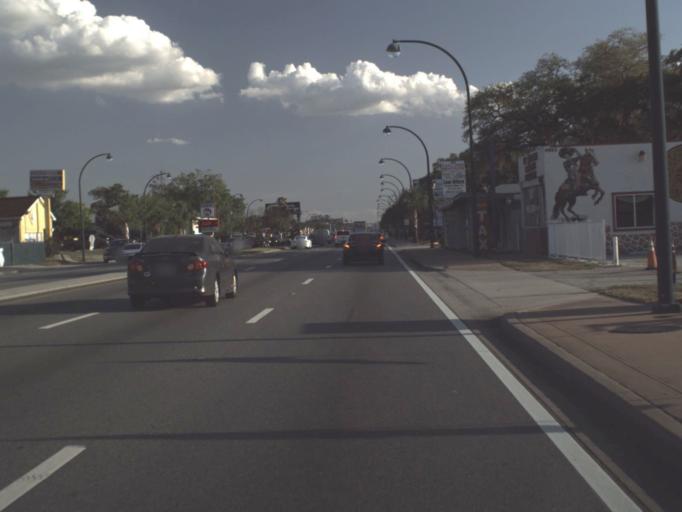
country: US
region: Florida
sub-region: Orange County
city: Holden Heights
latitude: 28.4904
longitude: -81.3969
